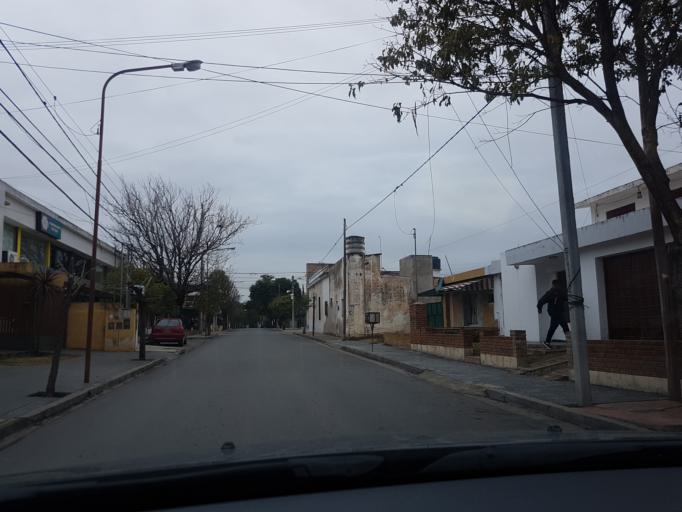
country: AR
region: Cordoba
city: Villa Allende
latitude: -31.2948
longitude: -64.2942
